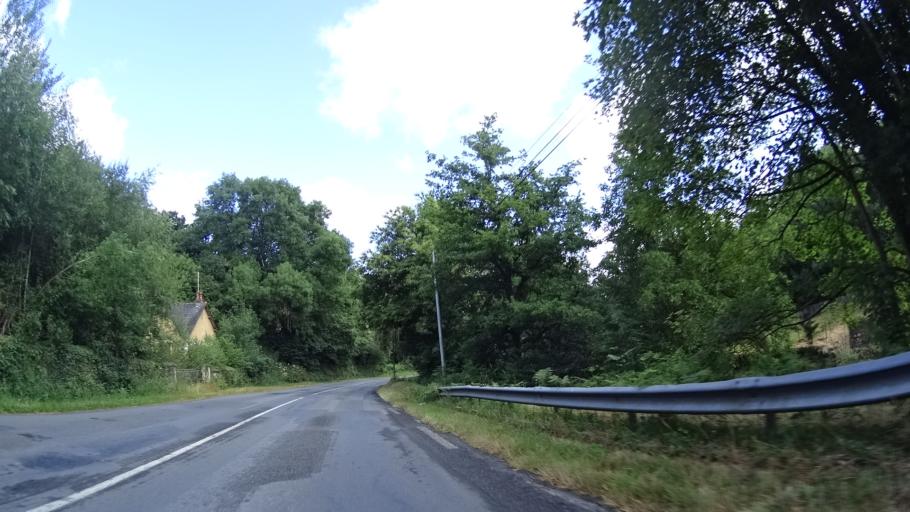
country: FR
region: Brittany
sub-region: Departement d'Ille-et-Vilaine
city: Hede-Bazouges
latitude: 48.2915
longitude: -1.8020
